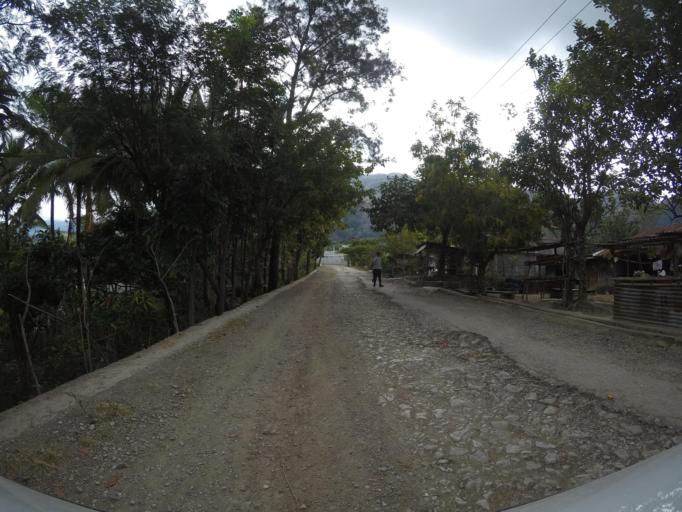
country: TL
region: Baucau
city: Baucau
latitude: -8.6282
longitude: 126.6564
